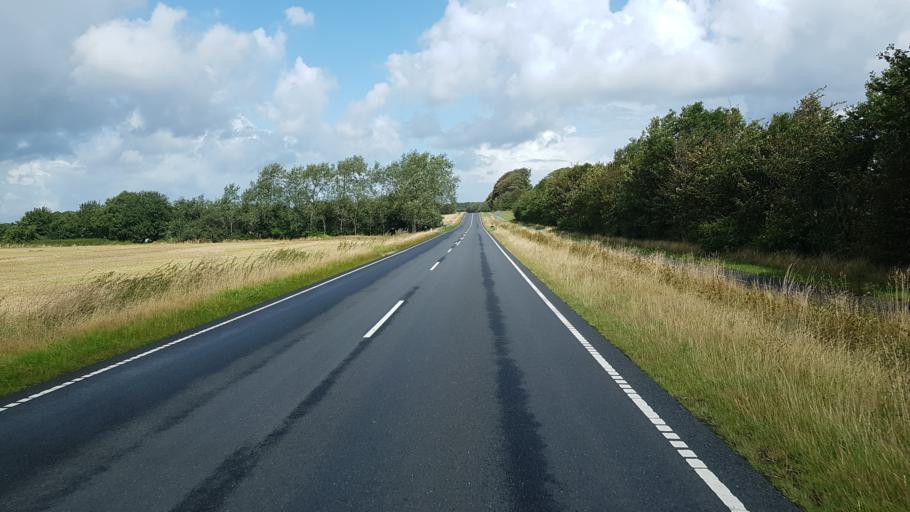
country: DK
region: South Denmark
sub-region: Vejen Kommune
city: Vejen
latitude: 55.5429
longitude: 9.1127
